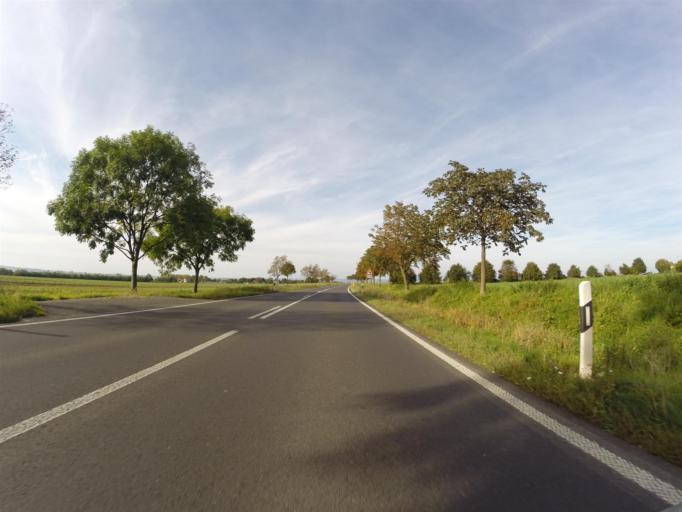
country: DE
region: Thuringia
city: Apolda
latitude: 50.9760
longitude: 11.5201
